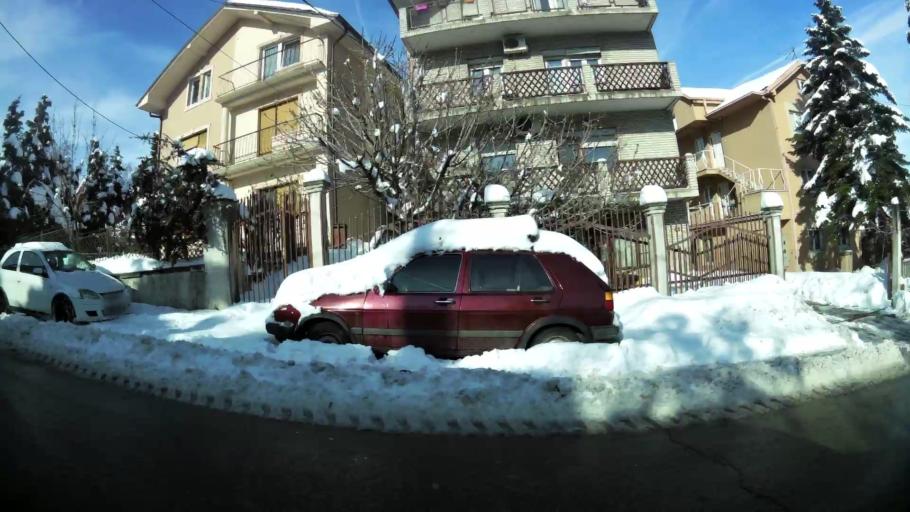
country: RS
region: Central Serbia
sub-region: Belgrade
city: Palilula
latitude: 44.7940
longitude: 20.5254
